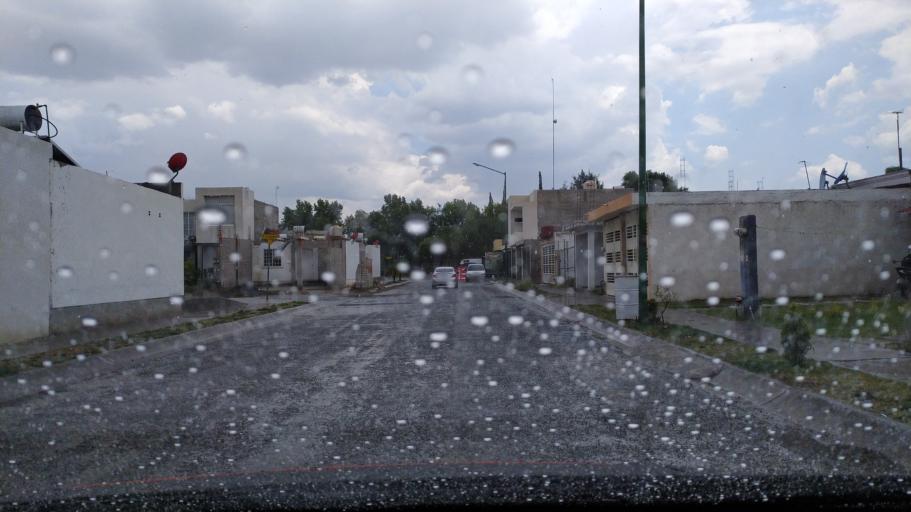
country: MX
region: Guanajuato
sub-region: San Francisco del Rincon
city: Estacion de San Francisco
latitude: 21.0282
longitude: -101.8290
